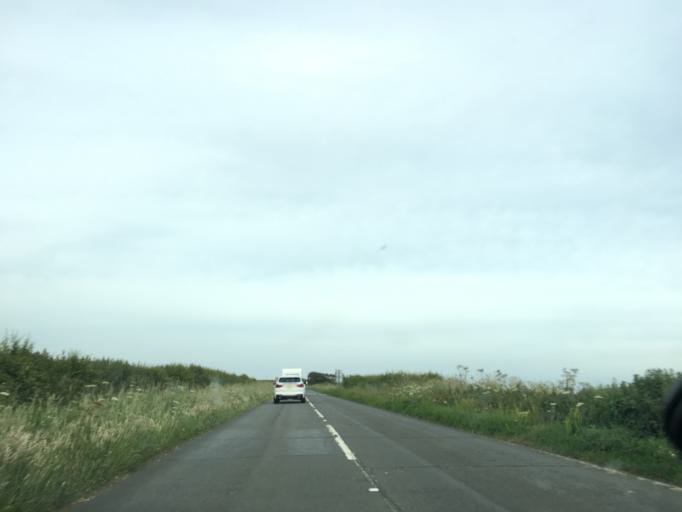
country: GB
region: England
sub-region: Isle of Wight
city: Shalfleet
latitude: 50.6397
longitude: -1.4252
